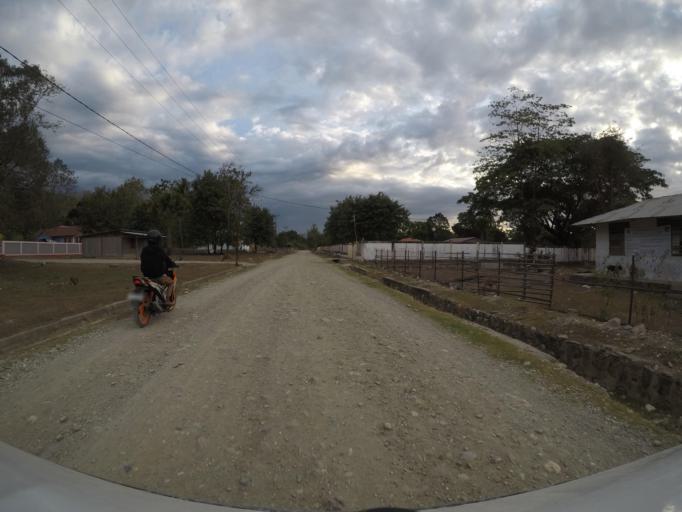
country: TL
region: Bobonaro
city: Maliana
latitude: -8.8807
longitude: 125.2109
